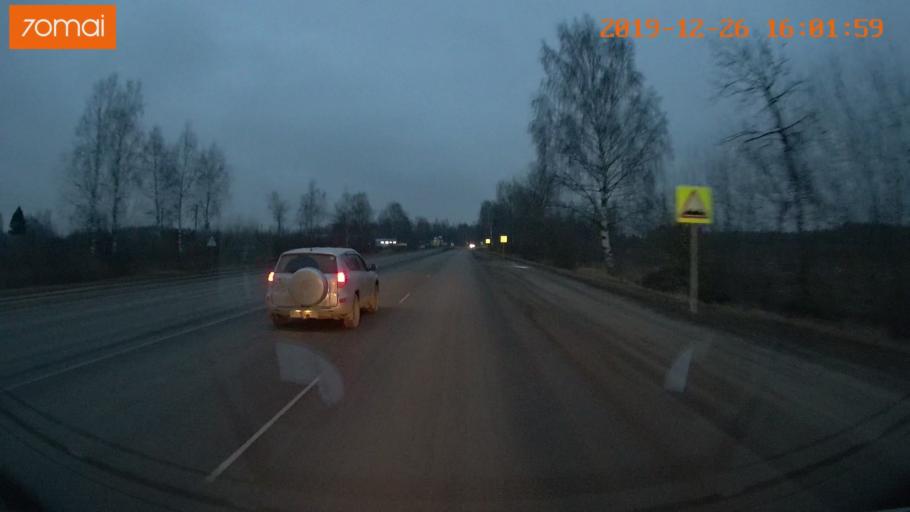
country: RU
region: Jaroslavl
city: Rybinsk
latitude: 58.0146
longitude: 38.8254
